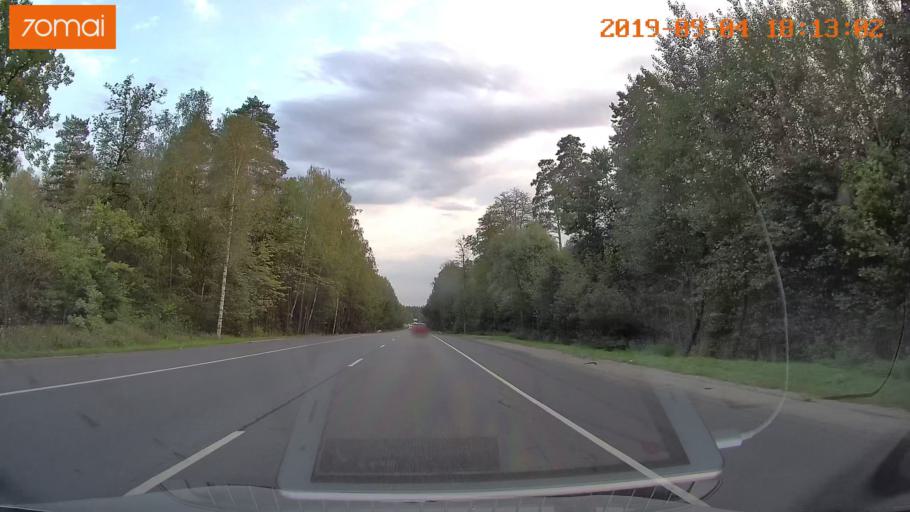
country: RU
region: Moskovskaya
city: Lopatinskiy
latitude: 55.3651
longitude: 38.7356
